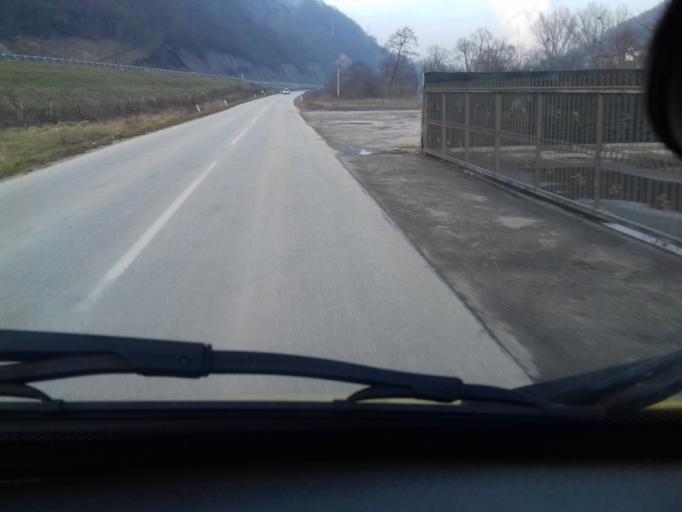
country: BA
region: Federation of Bosnia and Herzegovina
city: Dobrinje
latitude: 44.0576
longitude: 18.1037
